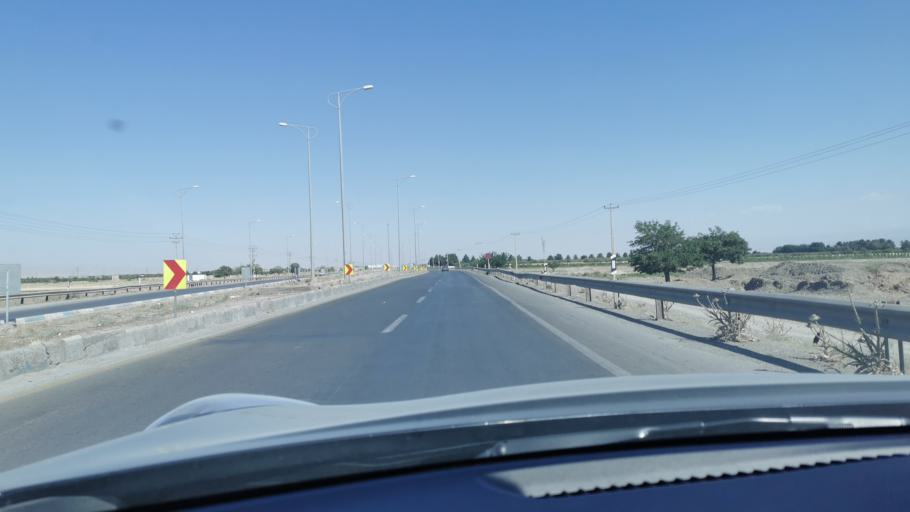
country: IR
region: Razavi Khorasan
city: Chenaran
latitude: 36.6217
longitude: 59.1530
